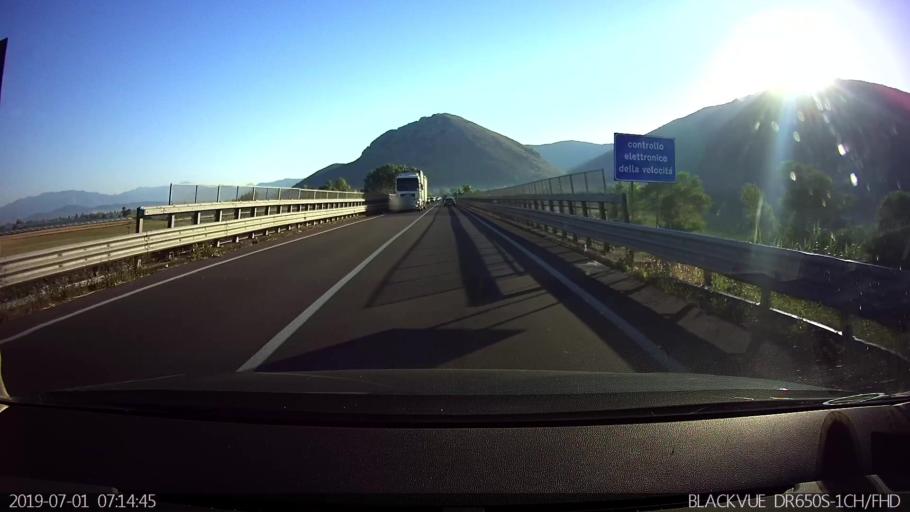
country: IT
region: Latium
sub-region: Provincia di Latina
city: Borgo Hermada
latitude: 41.3249
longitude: 13.1872
